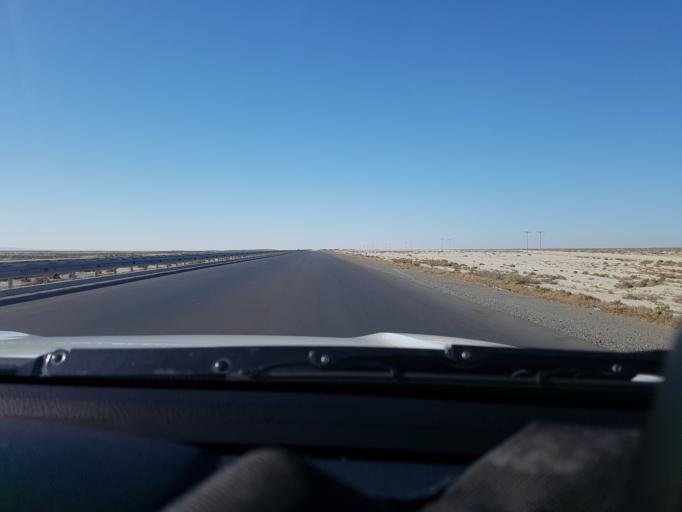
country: TM
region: Balkan
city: Gazanjyk
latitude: 39.2544
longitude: 55.1044
